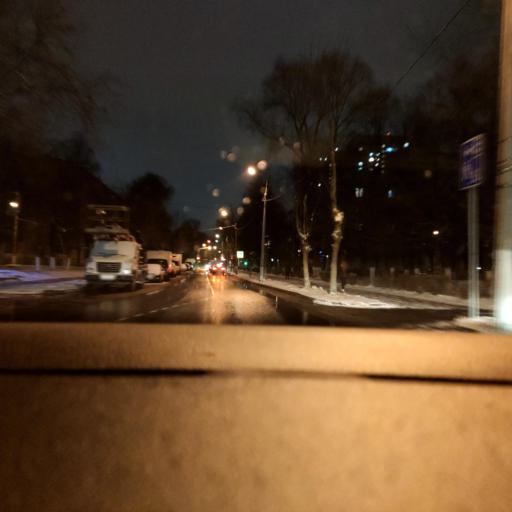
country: RU
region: Moskovskaya
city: Reutov
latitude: 55.7628
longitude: 37.8630
